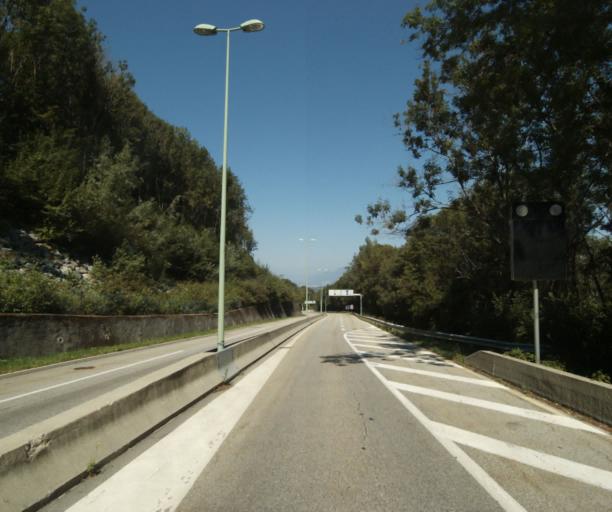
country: FR
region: Rhone-Alpes
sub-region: Departement de l'Isere
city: Notre-Dame-de-Mesage
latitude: 45.0333
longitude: 5.7687
